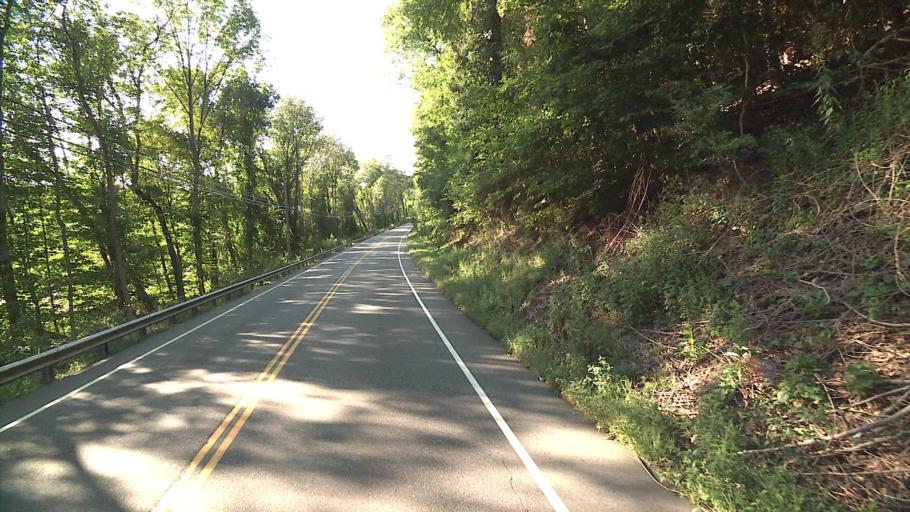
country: US
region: Connecticut
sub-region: New London County
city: Baltic
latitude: 41.6002
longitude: -72.1322
